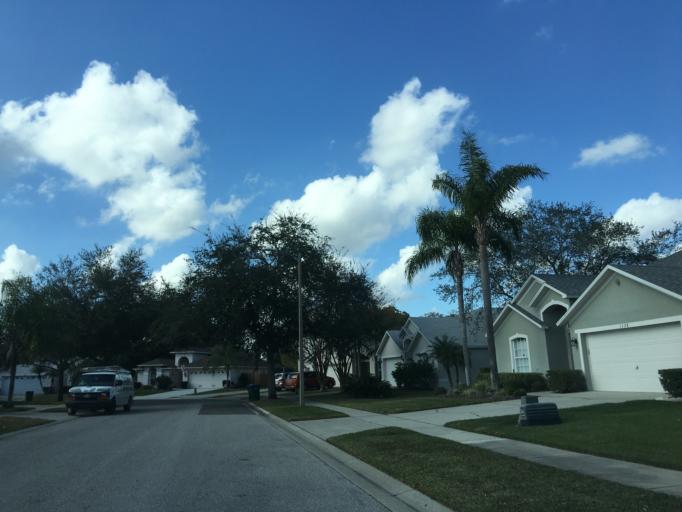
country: US
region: Florida
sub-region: Orange County
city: Eatonville
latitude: 28.6307
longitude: -81.4068
